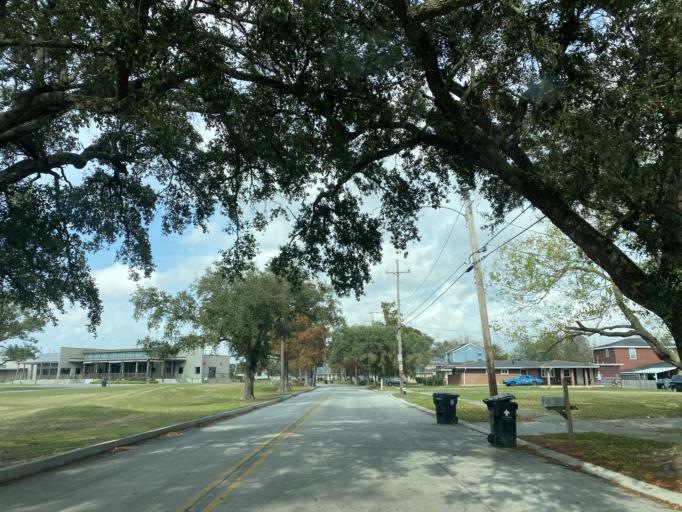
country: US
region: Louisiana
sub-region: Saint Bernard Parish
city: Arabi
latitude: 30.0262
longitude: -90.0384
